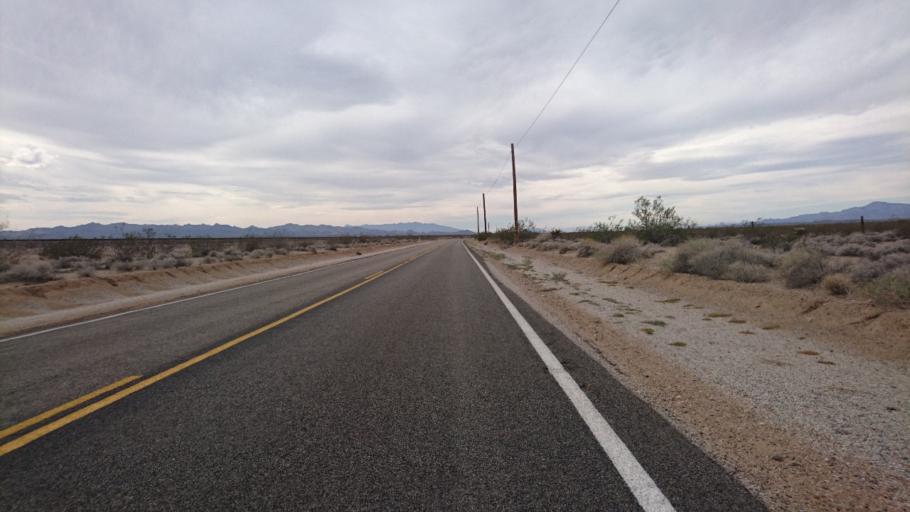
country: US
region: California
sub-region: San Bernardino County
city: Needles
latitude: 34.8891
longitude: -115.0978
